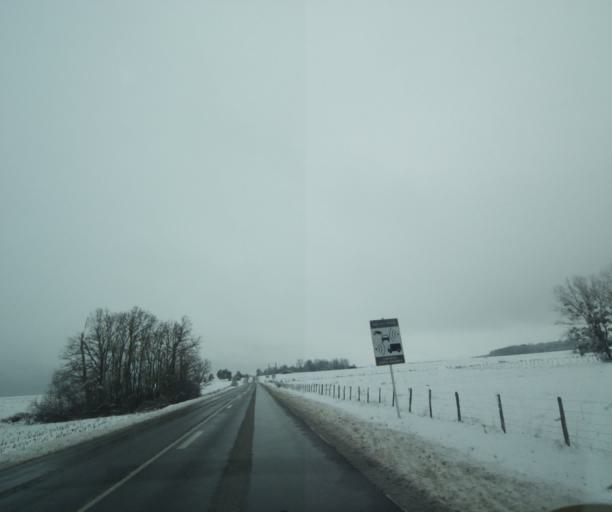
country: FR
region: Champagne-Ardenne
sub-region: Departement de la Haute-Marne
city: Montier-en-Der
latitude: 48.5264
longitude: 4.8141
